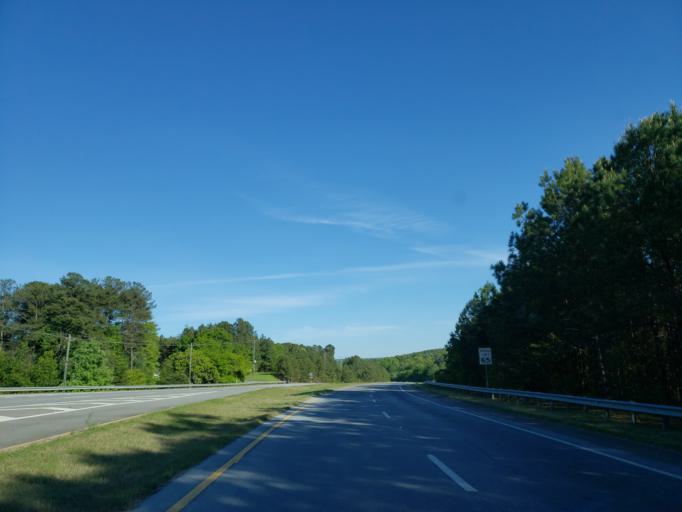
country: US
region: Georgia
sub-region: Polk County
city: Cedartown
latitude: 34.0098
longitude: -85.1788
